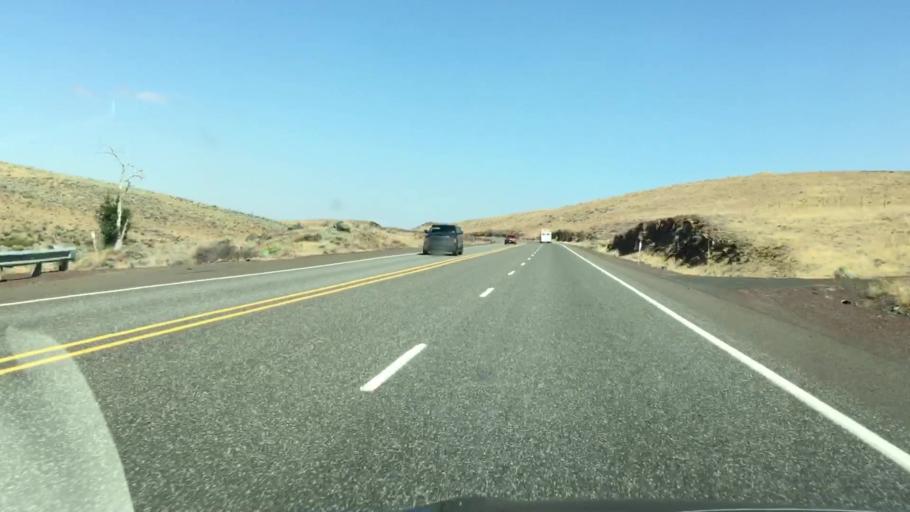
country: US
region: Oregon
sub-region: Wasco County
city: The Dalles
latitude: 45.3148
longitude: -121.1468
